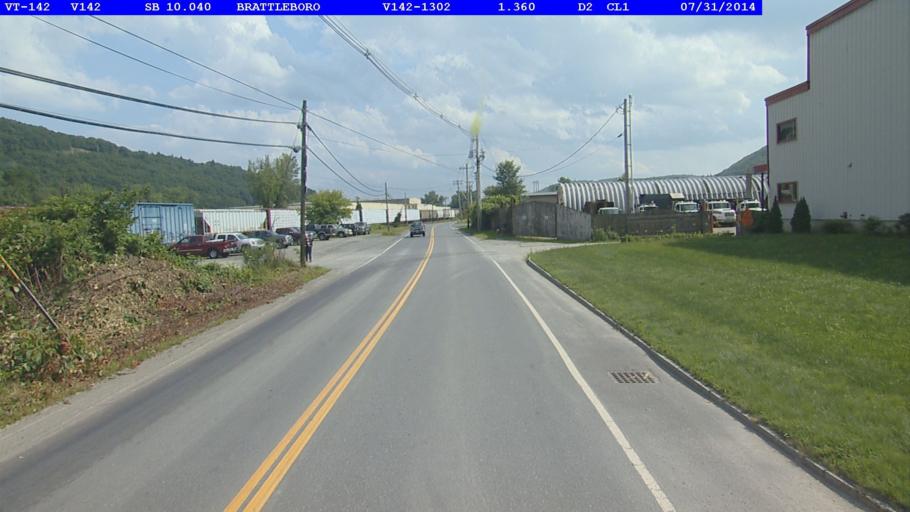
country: US
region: Vermont
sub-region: Windham County
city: Brattleboro
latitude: 42.8407
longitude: -72.5502
